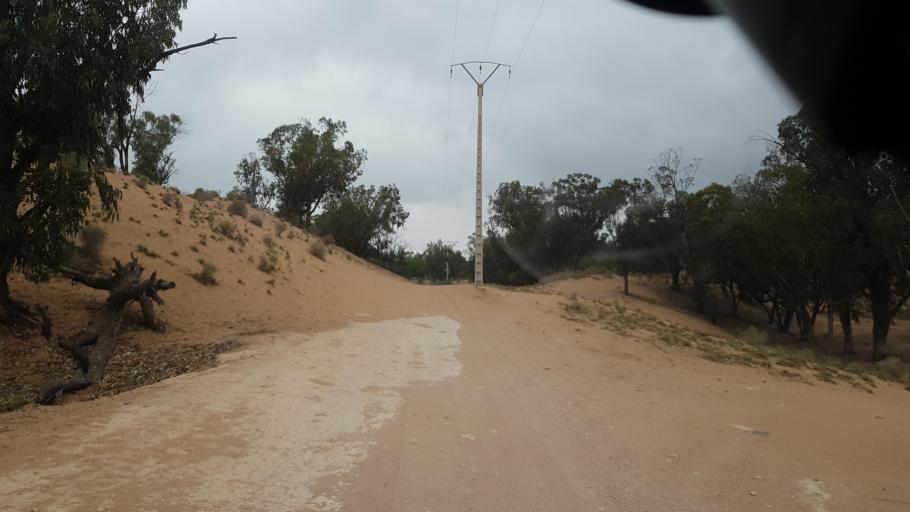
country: MA
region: Souss-Massa-Draa
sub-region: Inezgane-Ait Mellou
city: Inezgane
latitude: 30.3169
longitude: -9.5379
